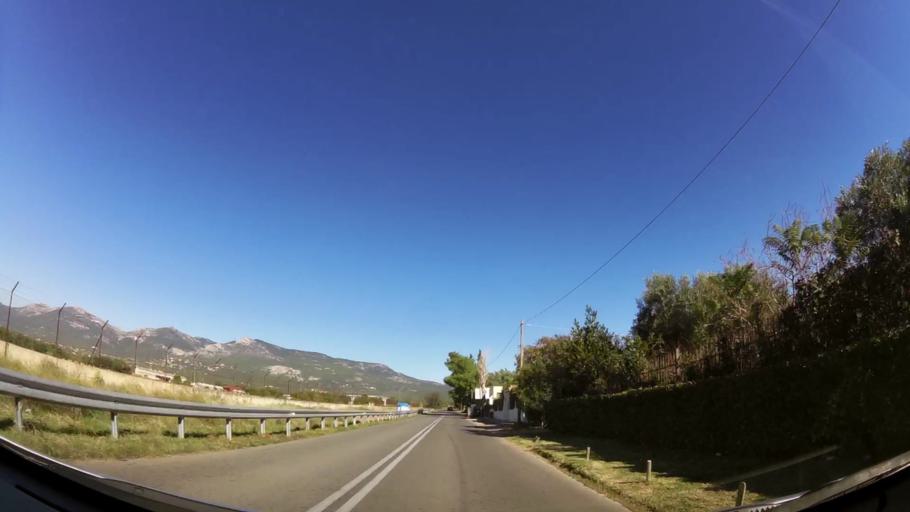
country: GR
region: Attica
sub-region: Nomarchia Anatolikis Attikis
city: Varybobi
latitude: 38.1136
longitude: 23.7899
